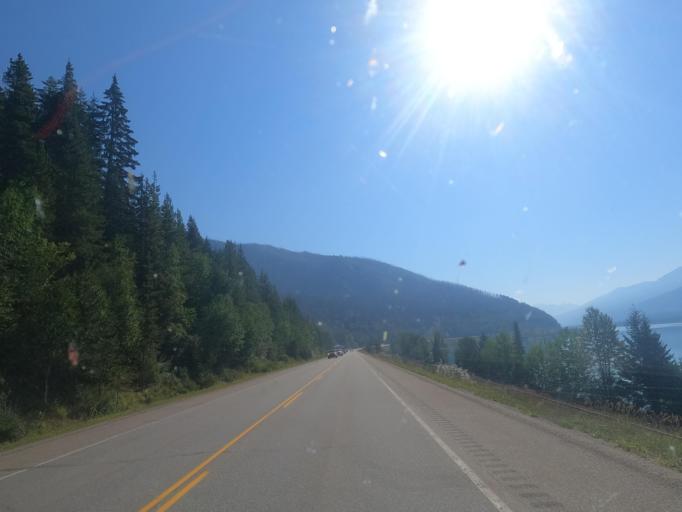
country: CA
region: Alberta
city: Jasper Park Lodge
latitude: 52.9535
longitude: -118.8768
